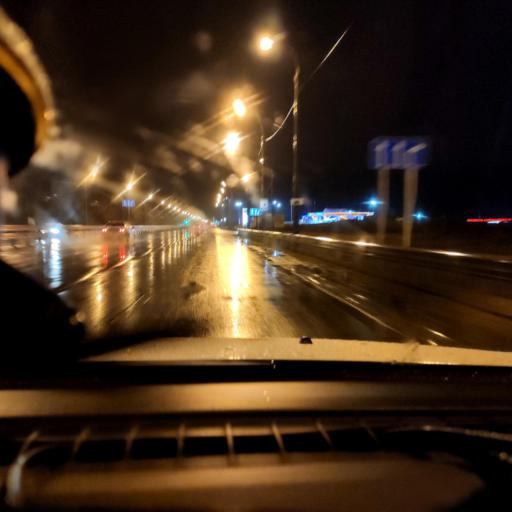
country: RU
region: Samara
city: Samara
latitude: 53.1154
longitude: 50.1664
